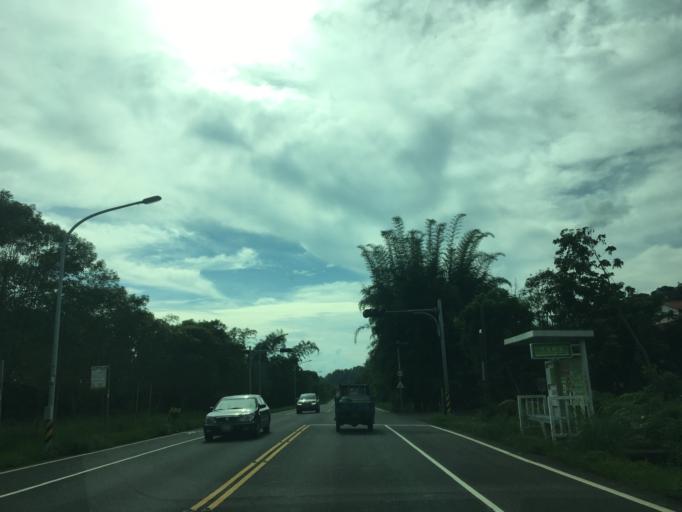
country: TW
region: Taiwan
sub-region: Chiayi
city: Jiayi Shi
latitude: 23.4500
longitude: 120.5717
